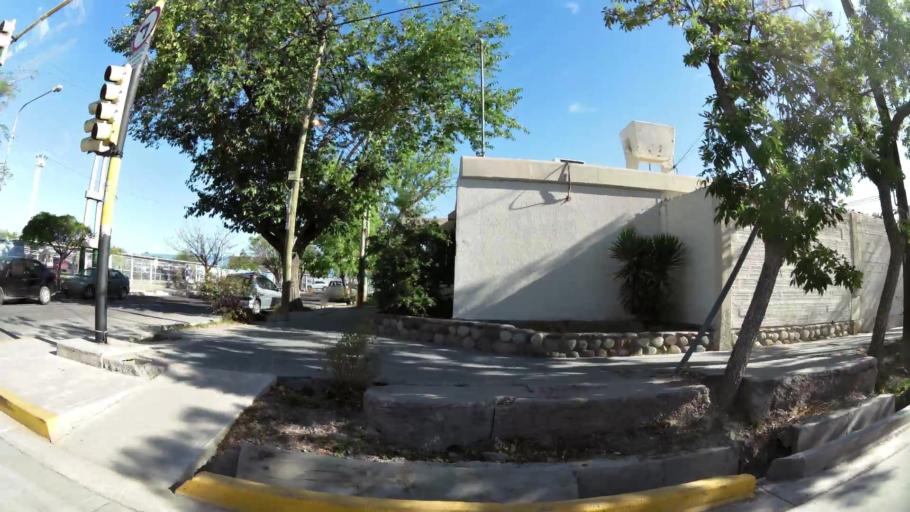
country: AR
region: Mendoza
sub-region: Departamento de Godoy Cruz
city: Godoy Cruz
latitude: -32.9140
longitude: -68.8265
